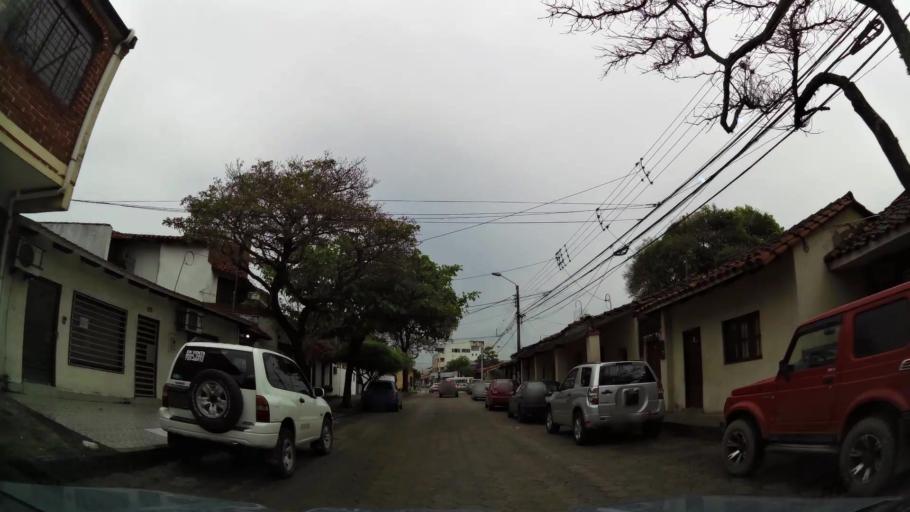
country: BO
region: Santa Cruz
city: Santa Cruz de la Sierra
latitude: -17.7861
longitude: -63.1745
